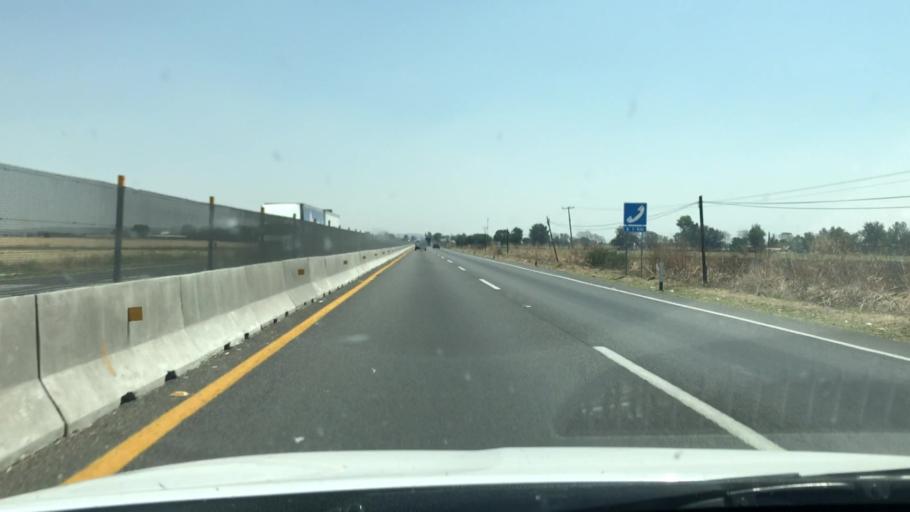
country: MX
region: Guanajuato
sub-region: Abasolo
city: San Bernardo Pena Blanca
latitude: 20.4807
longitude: -101.4958
